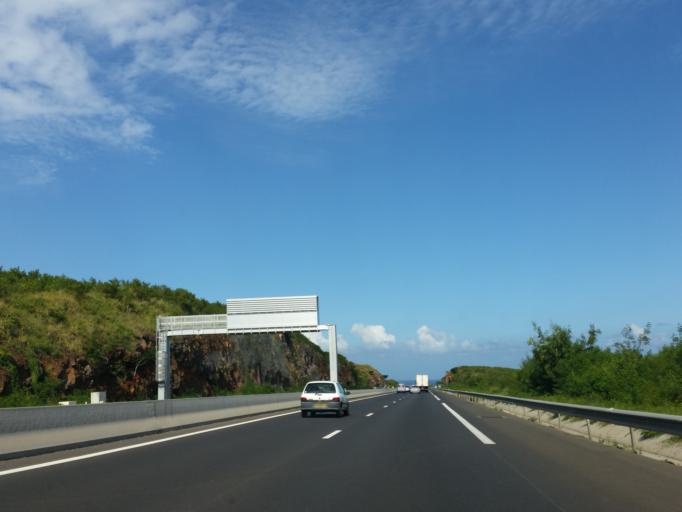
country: RE
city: Piton Saint-Leu
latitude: -21.2329
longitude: 55.3121
